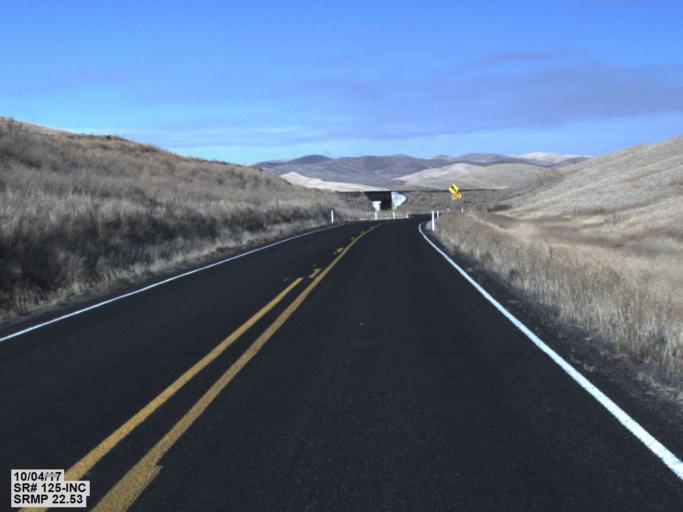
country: US
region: Washington
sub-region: Walla Walla County
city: Waitsburg
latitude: 46.2827
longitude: -118.3426
